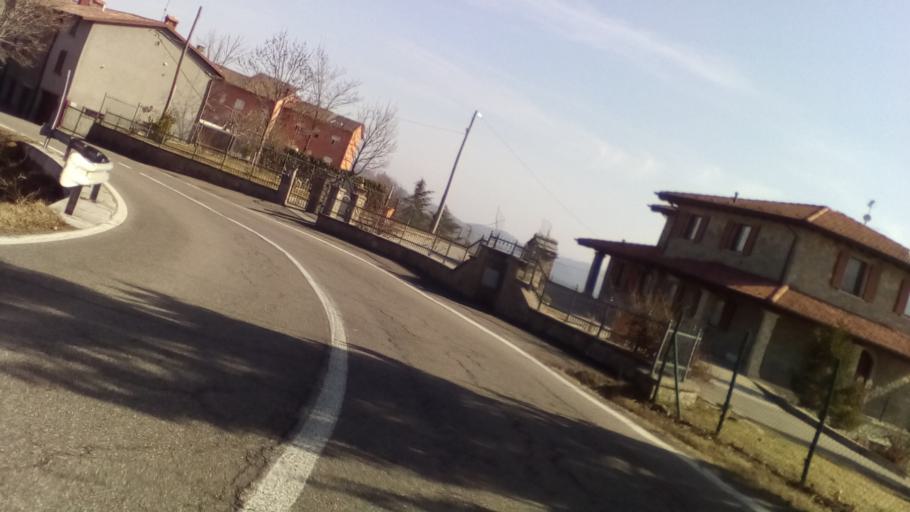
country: IT
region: Emilia-Romagna
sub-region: Provincia di Modena
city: Lama
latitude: 44.3126
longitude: 10.7569
